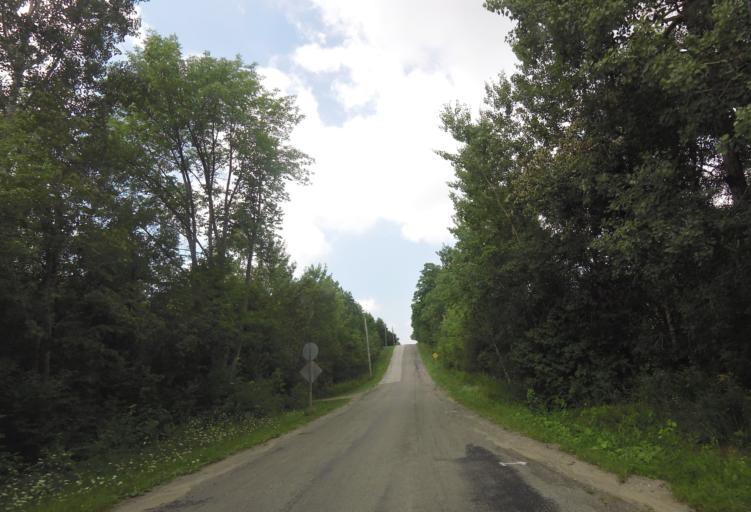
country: CA
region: Ontario
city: Oshawa
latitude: 43.9925
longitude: -78.8728
